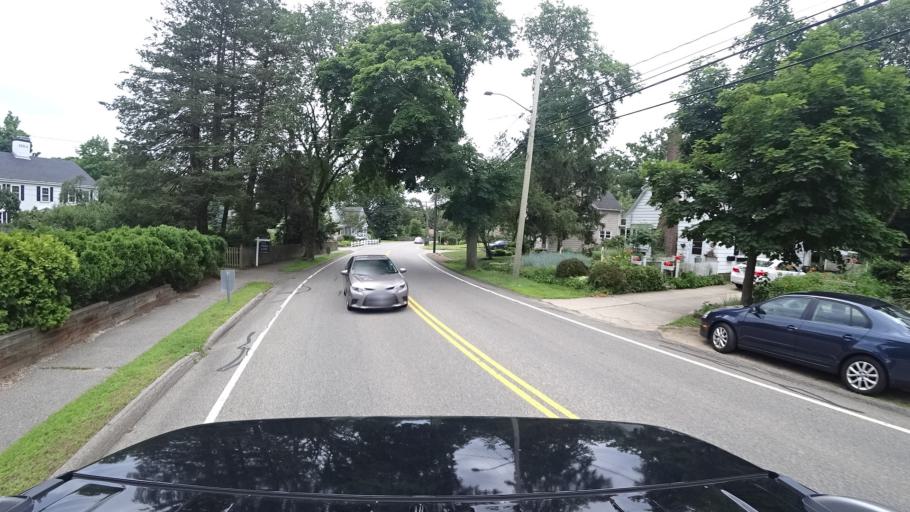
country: US
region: Massachusetts
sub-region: Norfolk County
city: Dedham
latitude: 42.2372
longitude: -71.1518
